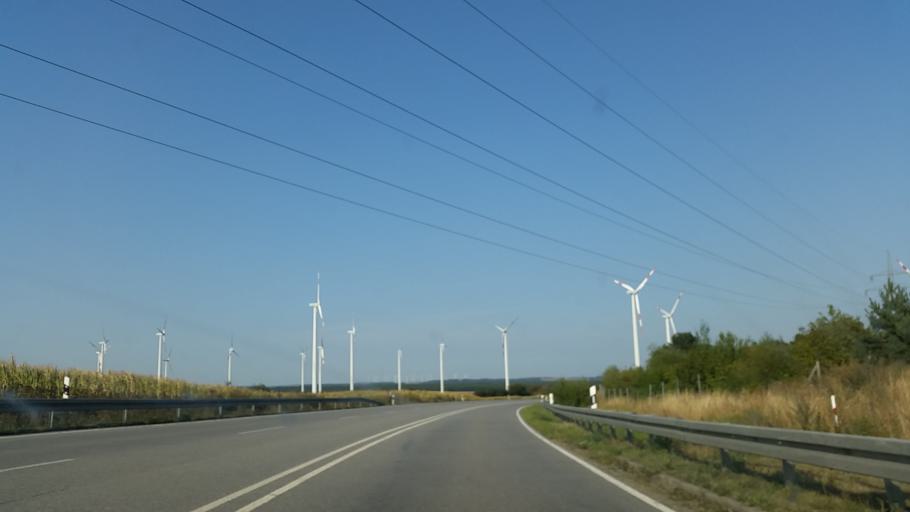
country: DE
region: Brandenburg
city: Meyenburg
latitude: 53.0817
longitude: 14.1731
